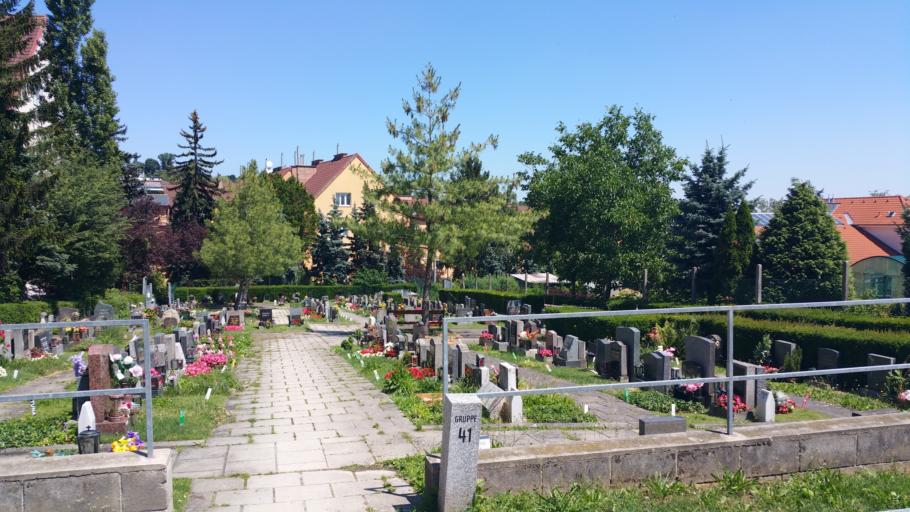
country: AT
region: Vienna
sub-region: Wien Stadt
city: Vienna
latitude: 48.2142
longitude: 16.2929
